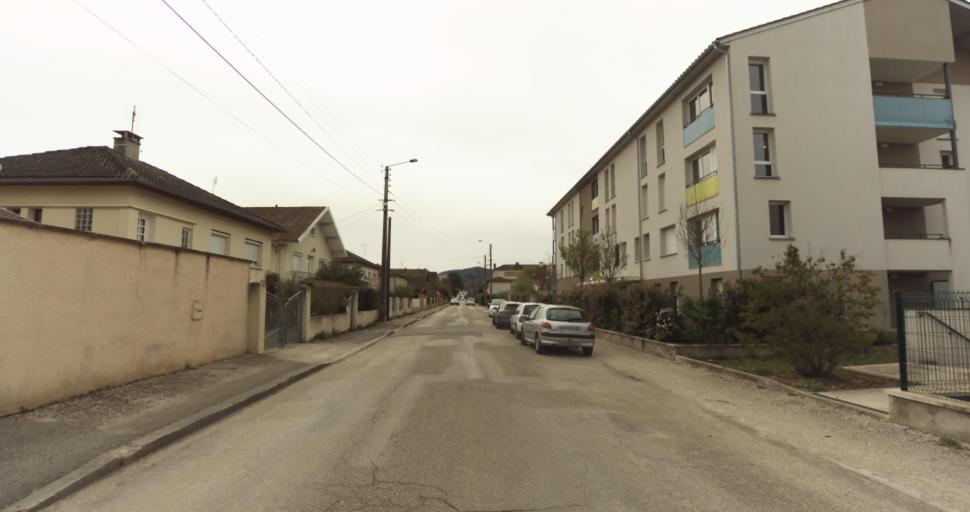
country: FR
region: Rhone-Alpes
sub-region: Departement de l'Ain
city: Amberieu-en-Bugey
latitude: 45.9648
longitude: 5.3536
